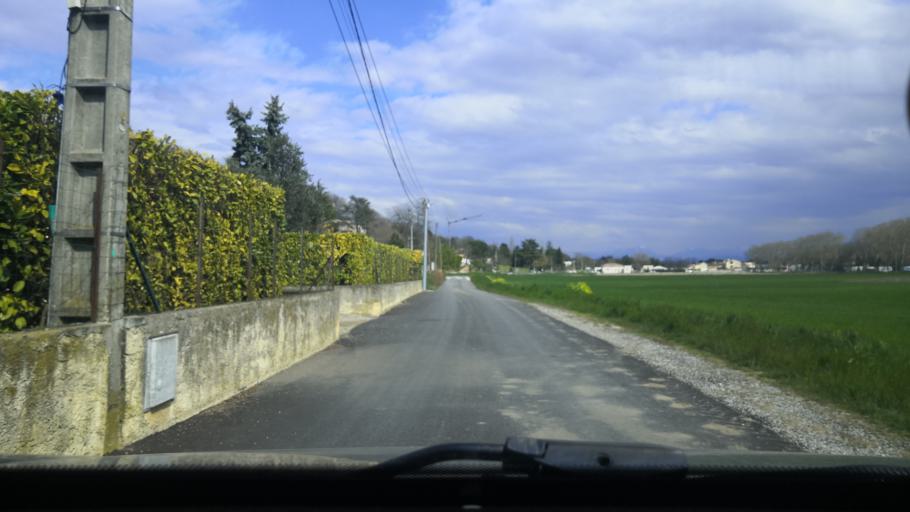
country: FR
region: Rhone-Alpes
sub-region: Departement de la Drome
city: Montelimar
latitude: 44.5646
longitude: 4.7631
